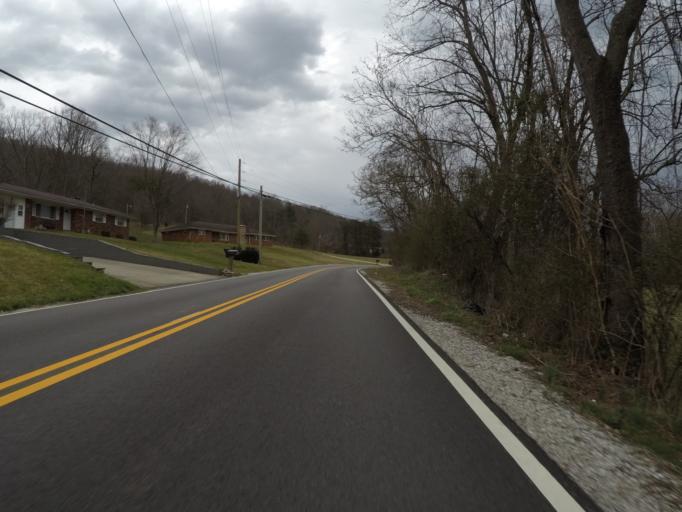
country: US
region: Ohio
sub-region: Lawrence County
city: Burlington
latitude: 38.4455
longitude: -82.5032
